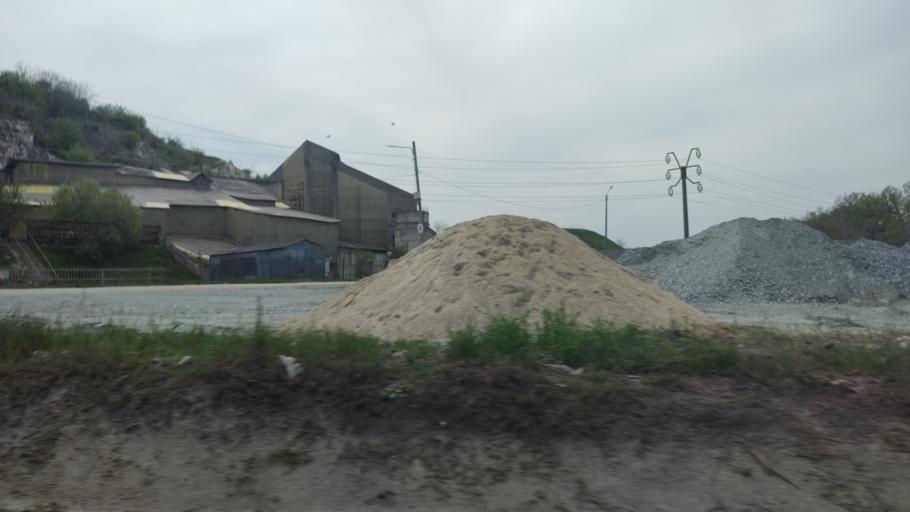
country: RO
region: Constanta
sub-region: Oras Murfatlar
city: Murfatlar
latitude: 44.1687
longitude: 28.4045
